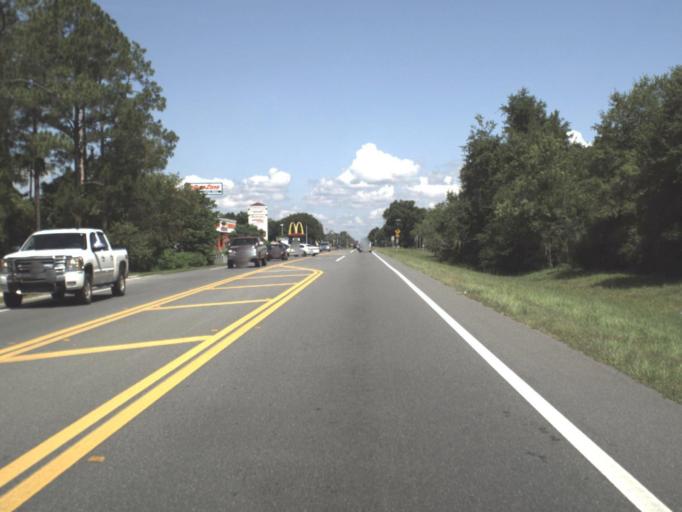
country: US
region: Florida
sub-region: Clay County
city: Keystone Heights
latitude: 29.7903
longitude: -82.0388
